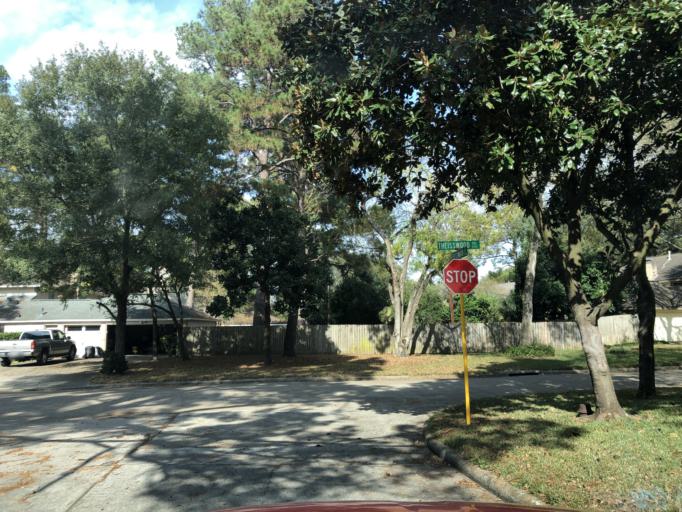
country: US
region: Texas
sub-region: Harris County
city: Tomball
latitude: 30.0249
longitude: -95.5465
